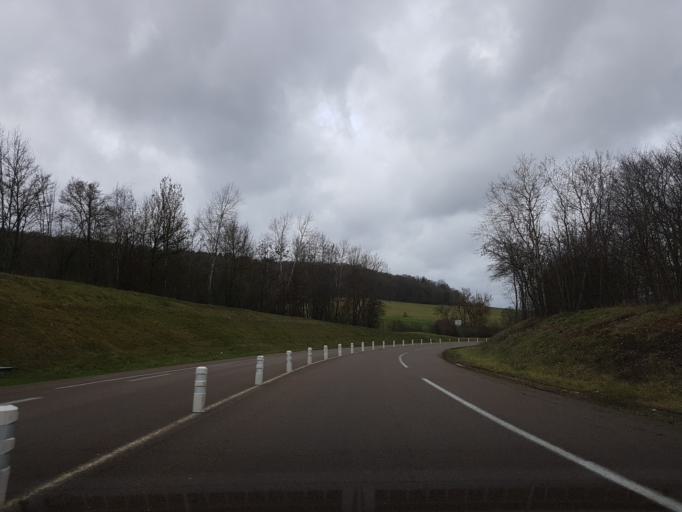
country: FR
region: Champagne-Ardenne
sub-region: Departement de la Haute-Marne
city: Rolampont
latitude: 47.9323
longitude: 5.2853
